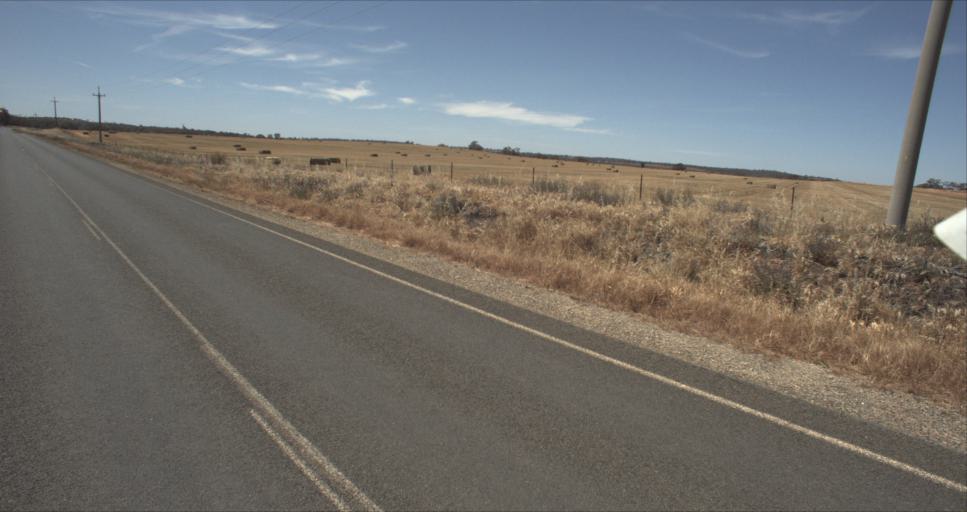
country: AU
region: New South Wales
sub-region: Leeton
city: Leeton
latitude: -34.6576
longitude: 146.4580
